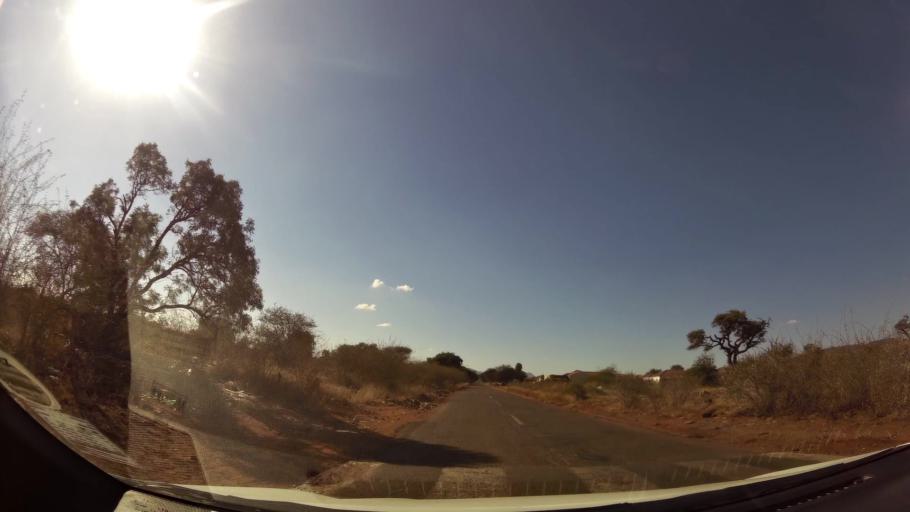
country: ZA
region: Limpopo
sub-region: Waterberg District Municipality
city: Mokopane
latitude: -24.2026
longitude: 28.9925
